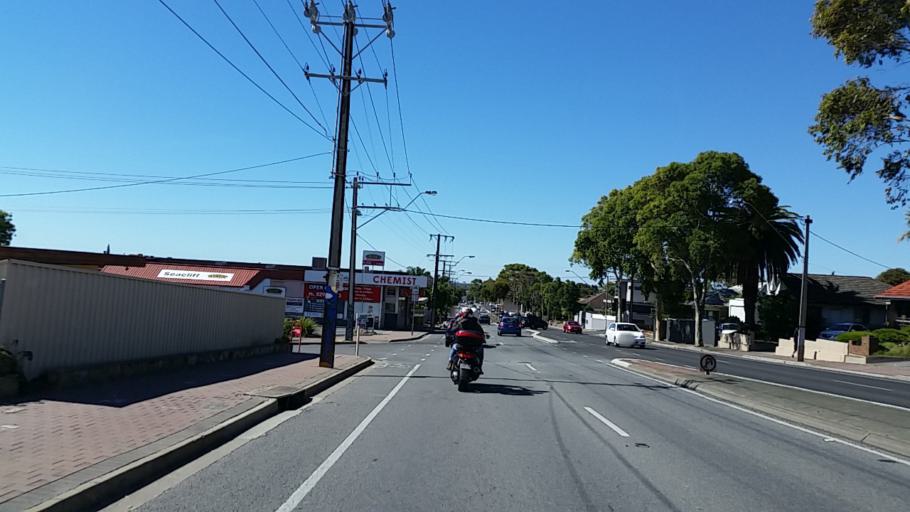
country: AU
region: South Australia
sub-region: Adelaide Hills
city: Seacliff
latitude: -35.0365
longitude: 138.5244
